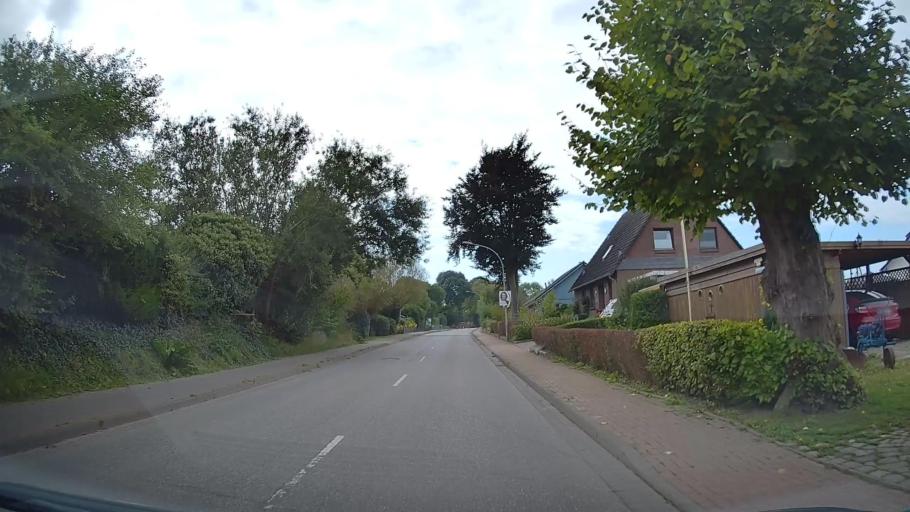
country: DE
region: Schleswig-Holstein
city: Panker
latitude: 54.3493
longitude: 10.6047
